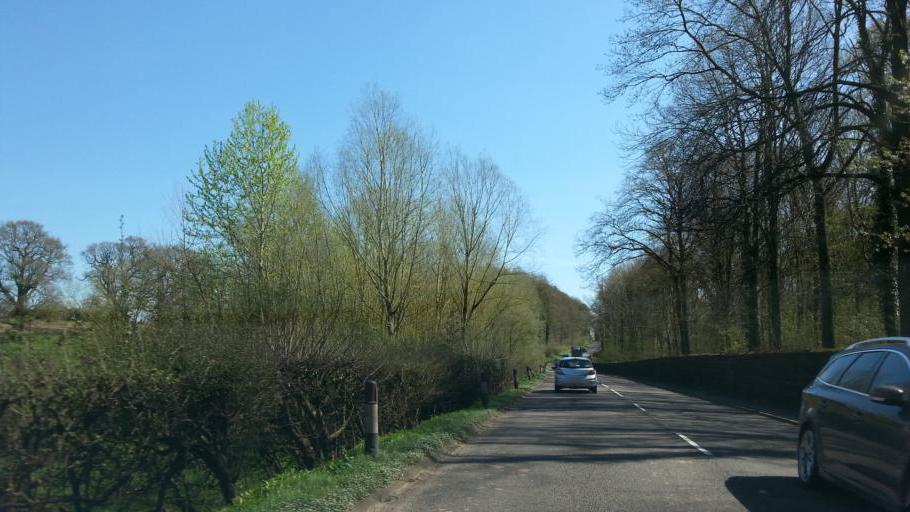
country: GB
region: England
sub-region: Shropshire
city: Tong
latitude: 52.6945
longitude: -2.2692
